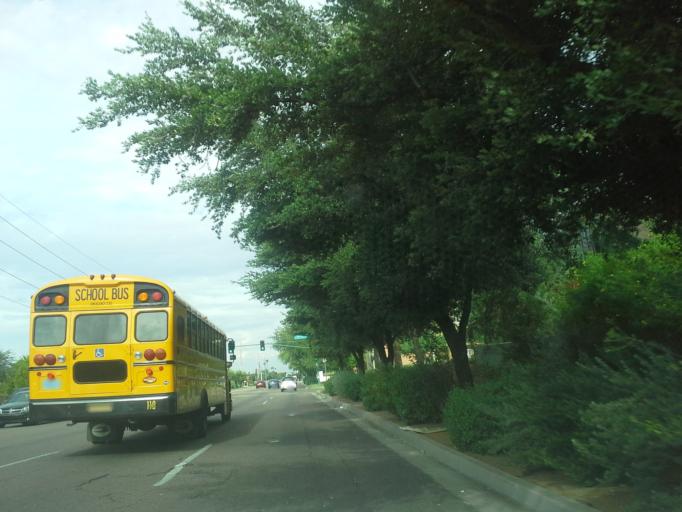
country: US
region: Arizona
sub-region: Maricopa County
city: Phoenix
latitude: 33.4805
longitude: -112.0860
